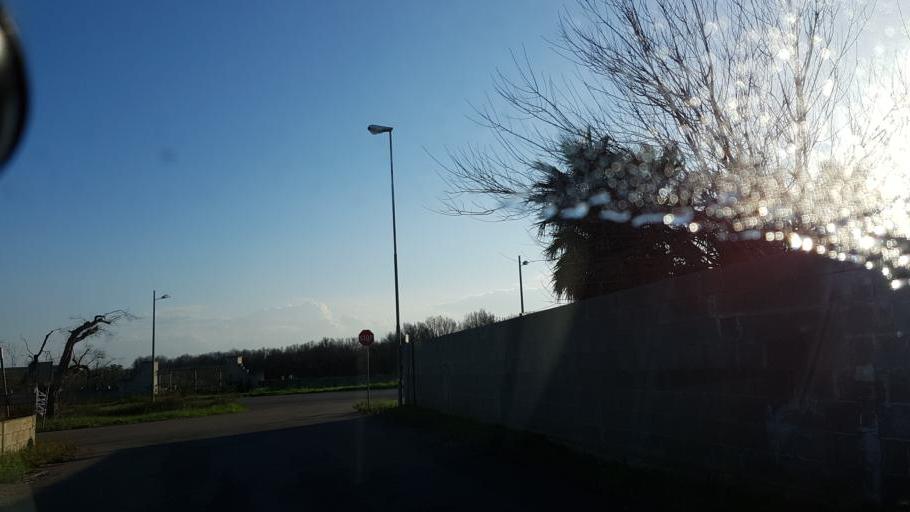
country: IT
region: Apulia
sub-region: Provincia di Brindisi
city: Torchiarolo
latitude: 40.5086
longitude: 18.0918
